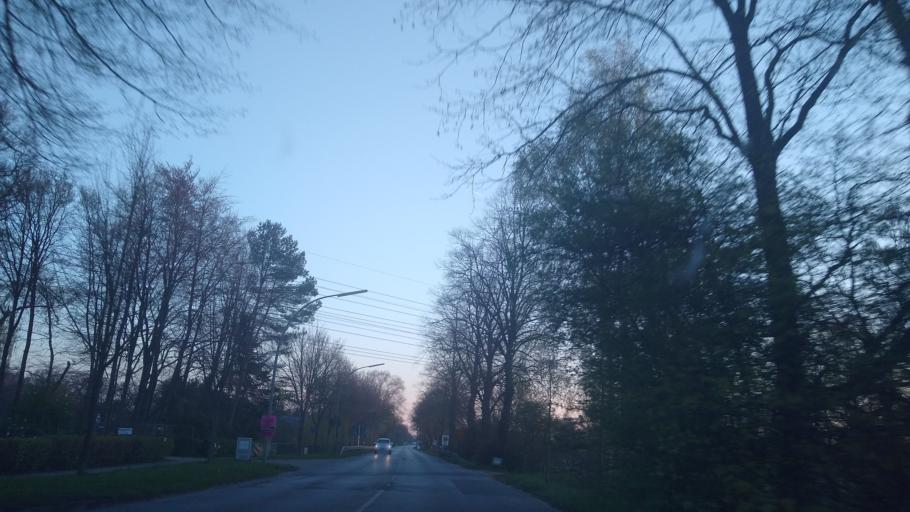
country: DE
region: Schleswig-Holstein
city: Bonningstedt
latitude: 53.6519
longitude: 9.9073
